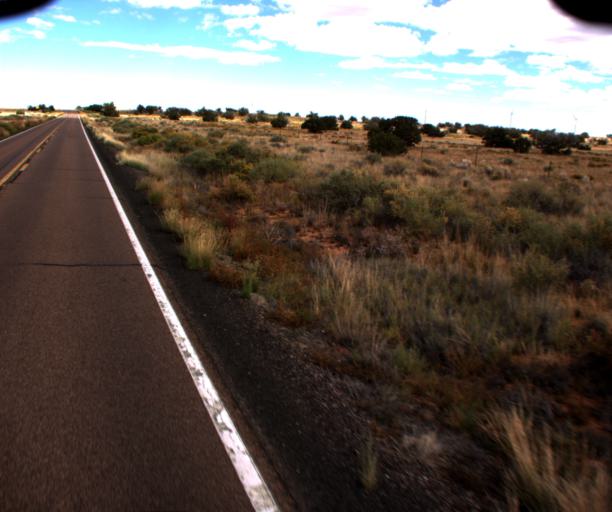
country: US
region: Arizona
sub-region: Navajo County
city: Snowflake
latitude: 34.6608
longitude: -110.3302
